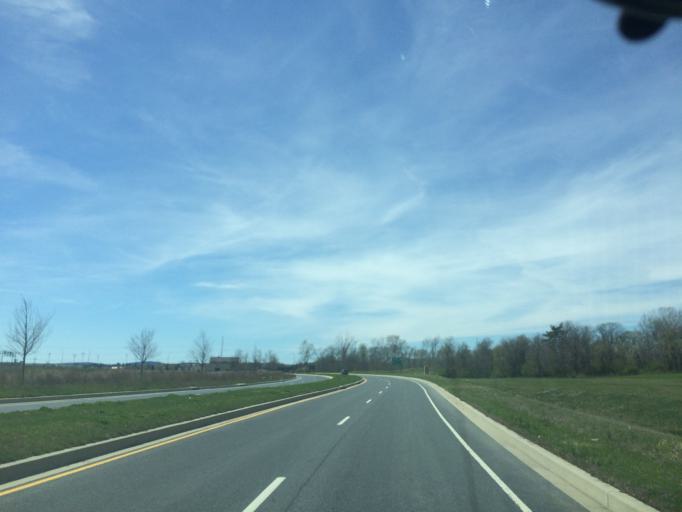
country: US
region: Maryland
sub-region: Frederick County
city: Frederick
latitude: 39.4038
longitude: -77.3983
